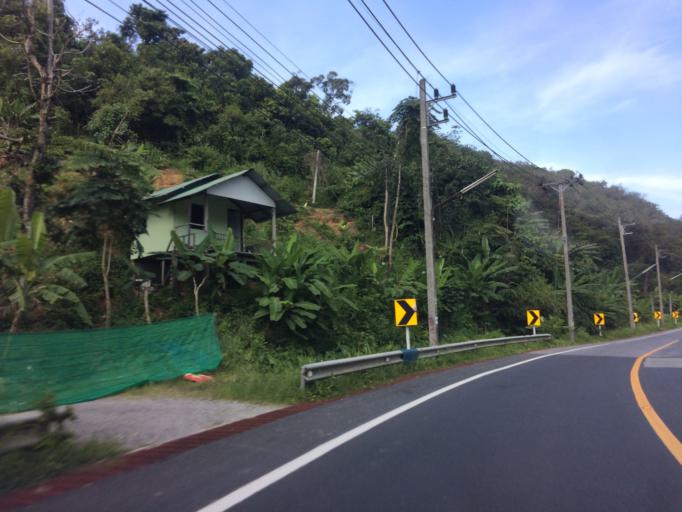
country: TH
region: Phuket
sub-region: Amphoe Kathu
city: Kathu
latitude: 7.9372
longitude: 98.3491
